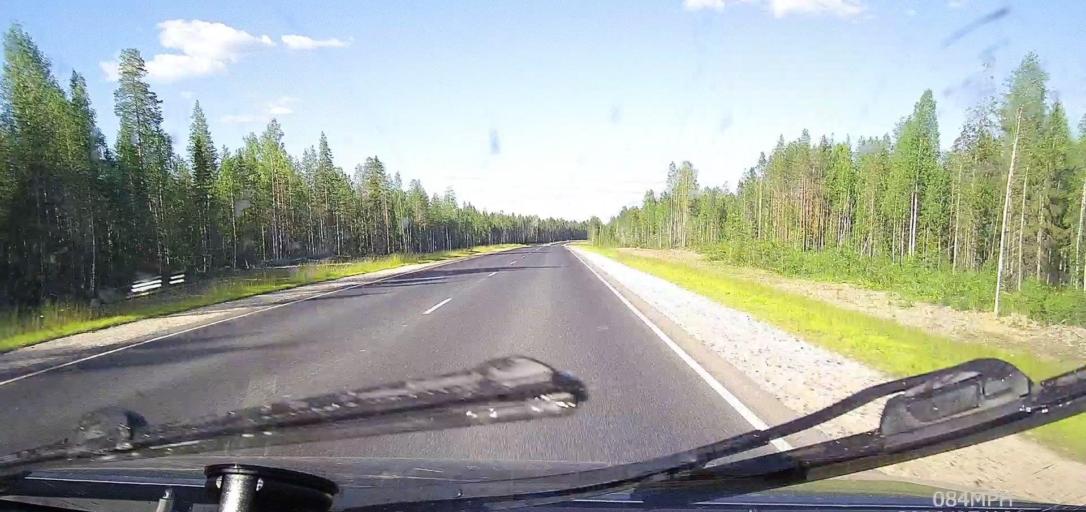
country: RU
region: Arkhangelskaya
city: Yemtsa
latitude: 63.1482
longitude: 40.4994
